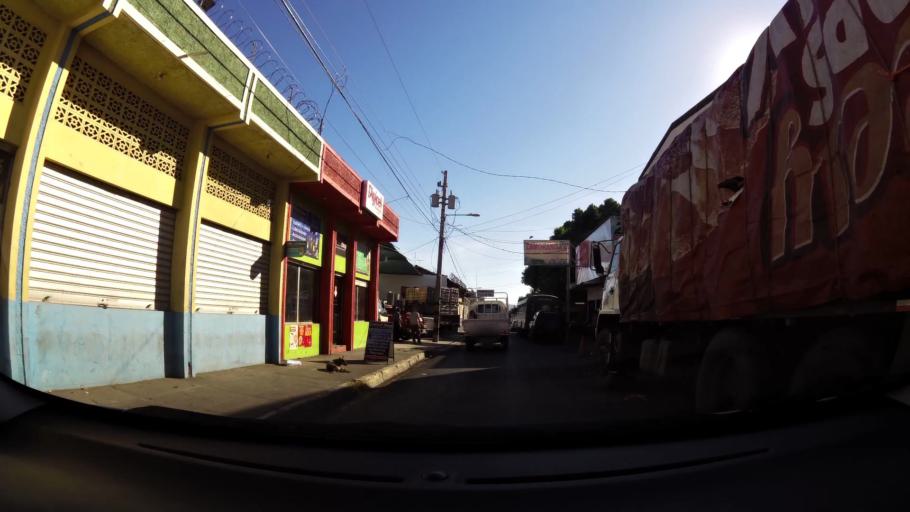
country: SV
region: San Miguel
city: San Miguel
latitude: 13.4788
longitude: -88.1770
